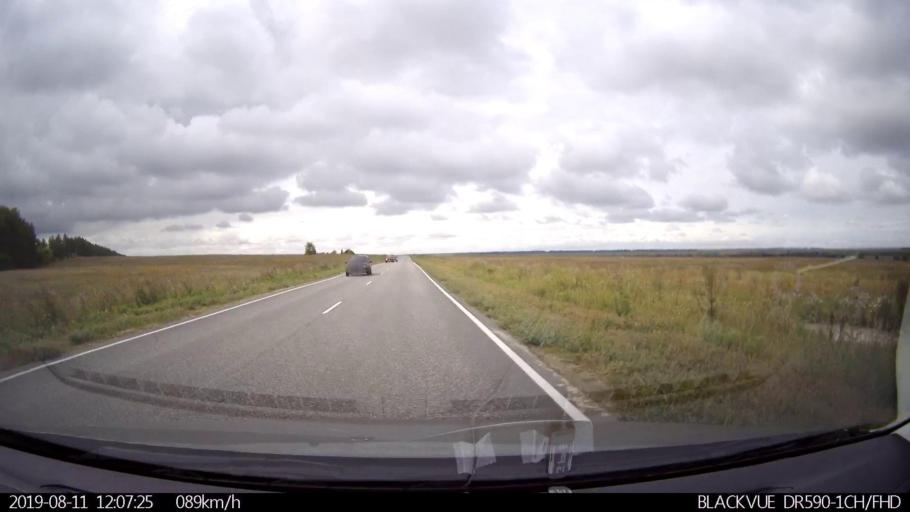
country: RU
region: Ulyanovsk
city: Silikatnyy
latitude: 53.9967
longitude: 48.0950
